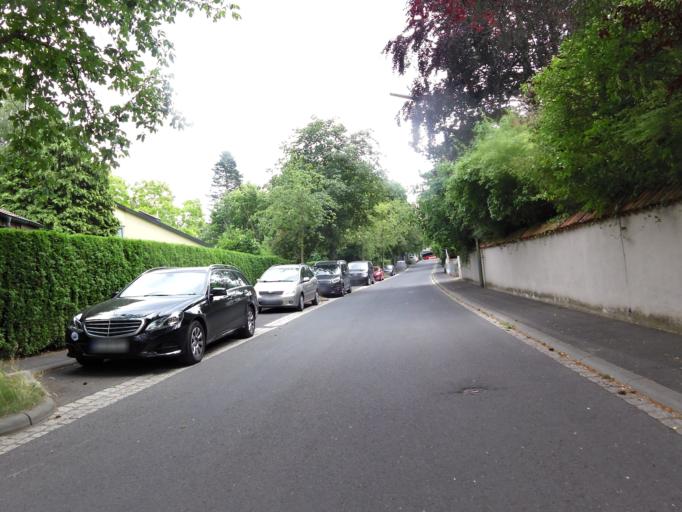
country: DE
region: Bavaria
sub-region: Regierungsbezirk Unterfranken
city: Wuerzburg
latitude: 49.7705
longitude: 9.9306
